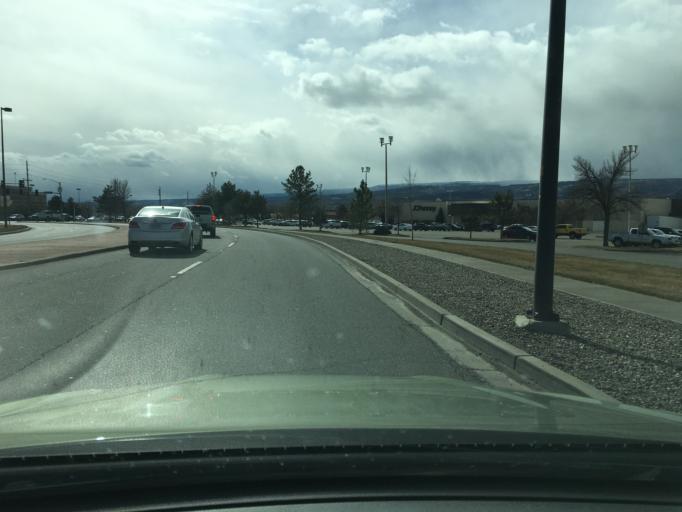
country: US
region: Colorado
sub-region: Mesa County
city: Redlands
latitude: 39.0929
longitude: -108.5997
